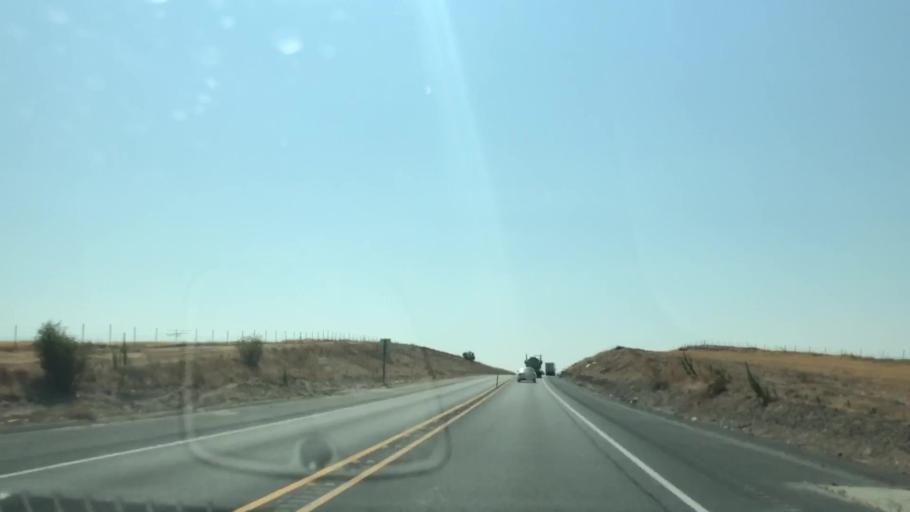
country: US
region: California
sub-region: Solano County
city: Suisun
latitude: 38.2140
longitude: -121.8828
